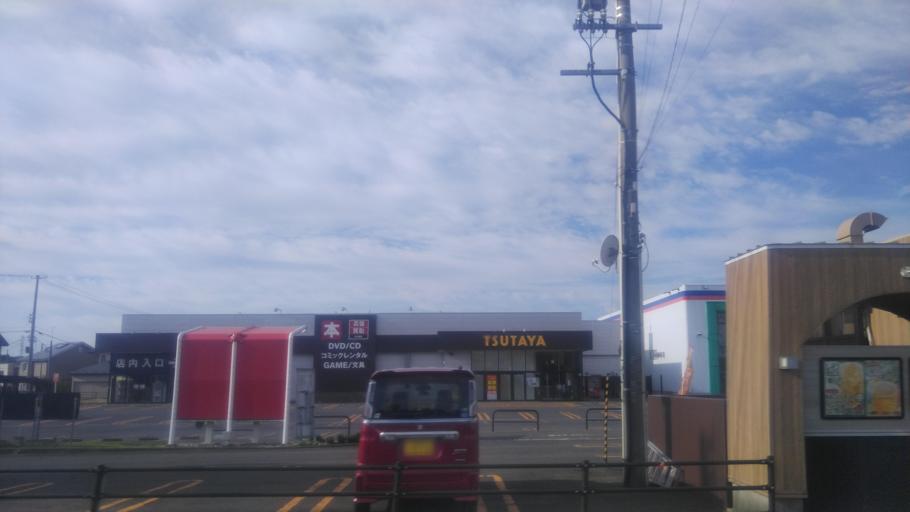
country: JP
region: Akita
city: Noshiromachi
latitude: 40.1881
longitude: 140.0415
